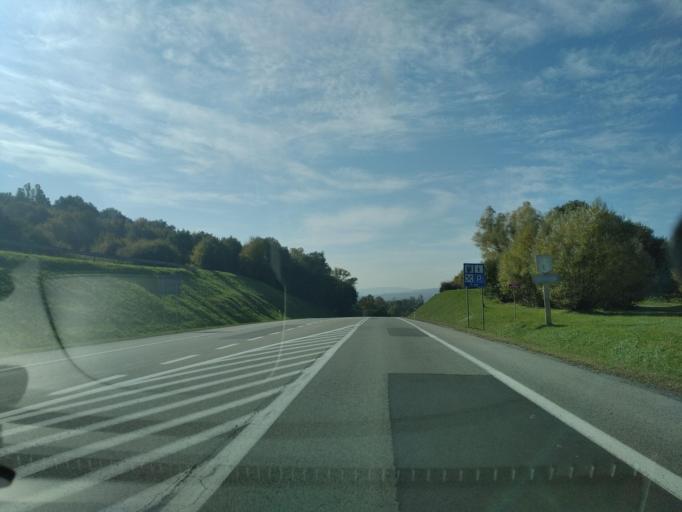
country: PL
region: Subcarpathian Voivodeship
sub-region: Powiat krosnienski
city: Miejsce Piastowe
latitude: 49.6065
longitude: 21.7376
